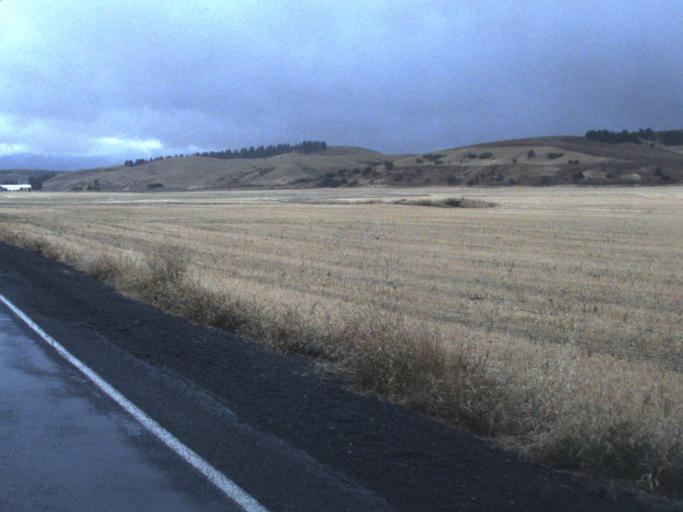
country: US
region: Washington
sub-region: Whitman County
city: Colfax
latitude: 47.0580
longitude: -117.5216
